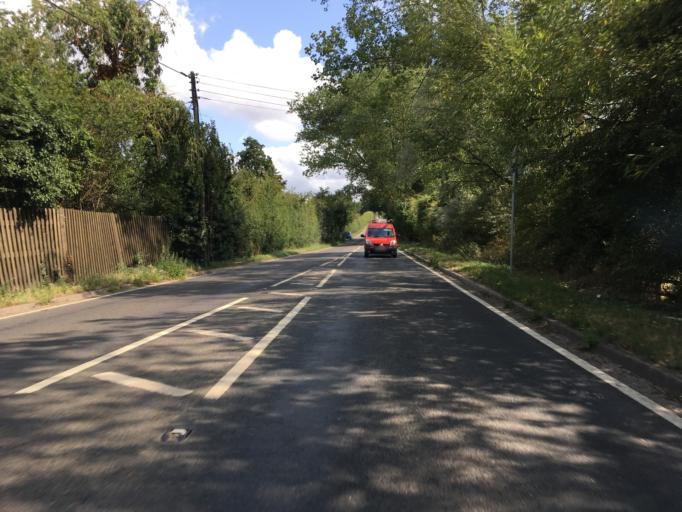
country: GB
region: England
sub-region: Kent
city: Headcorn
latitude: 51.1980
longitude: 0.5966
